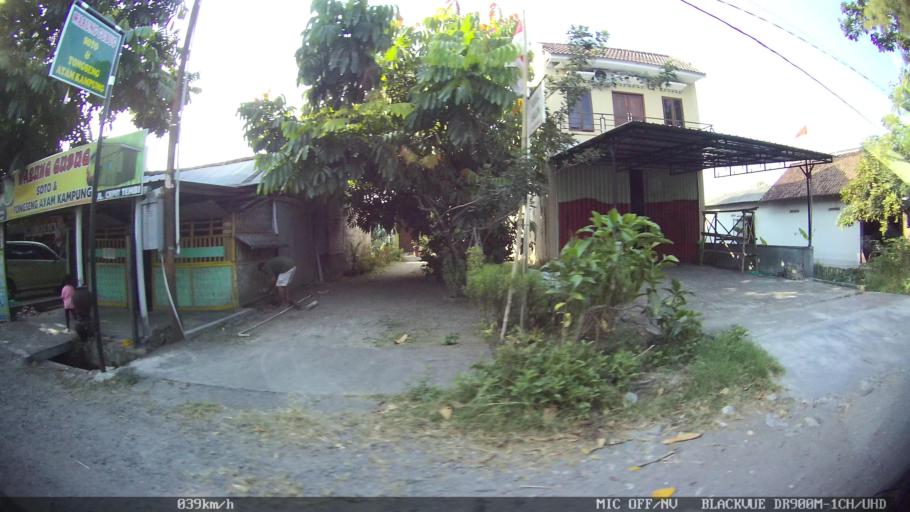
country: ID
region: Daerah Istimewa Yogyakarta
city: Sewon
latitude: -7.8670
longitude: 110.3405
